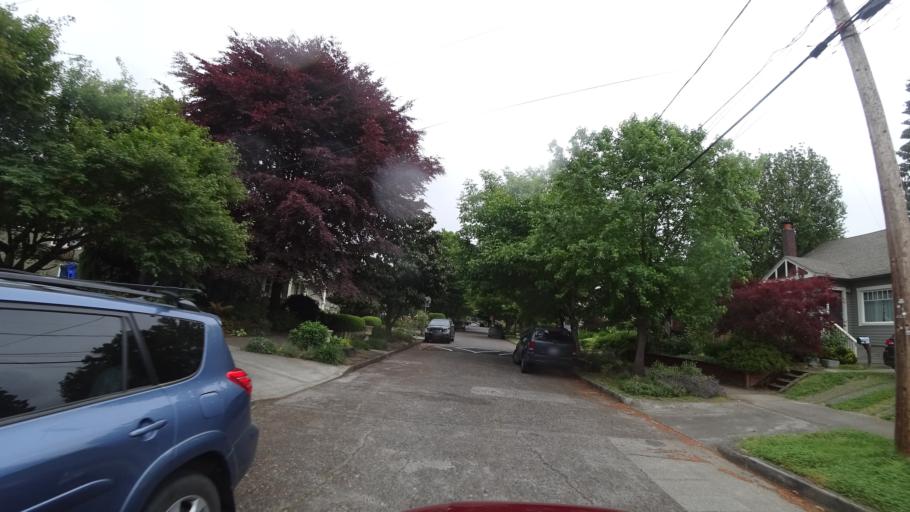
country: US
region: Oregon
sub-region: Clackamas County
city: Milwaukie
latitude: 45.4615
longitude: -122.6516
